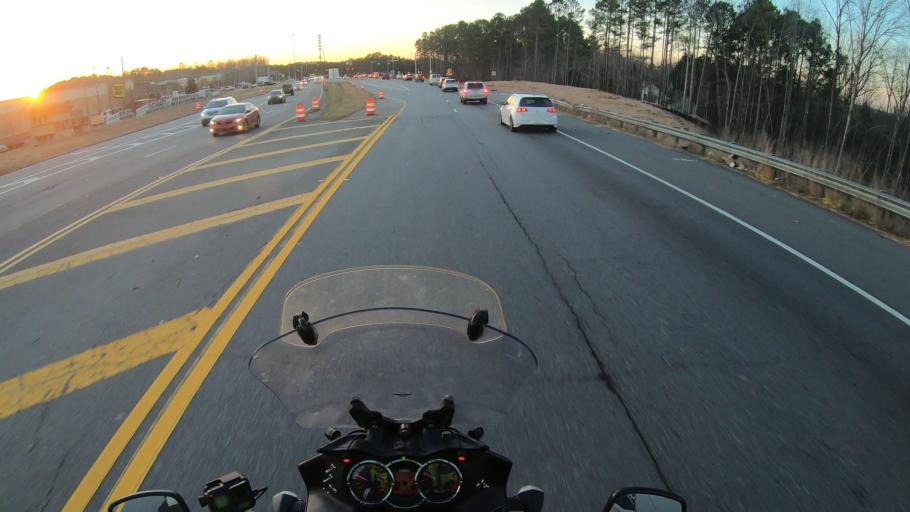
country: US
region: Georgia
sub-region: Cherokee County
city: Canton
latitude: 34.2377
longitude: -84.4604
